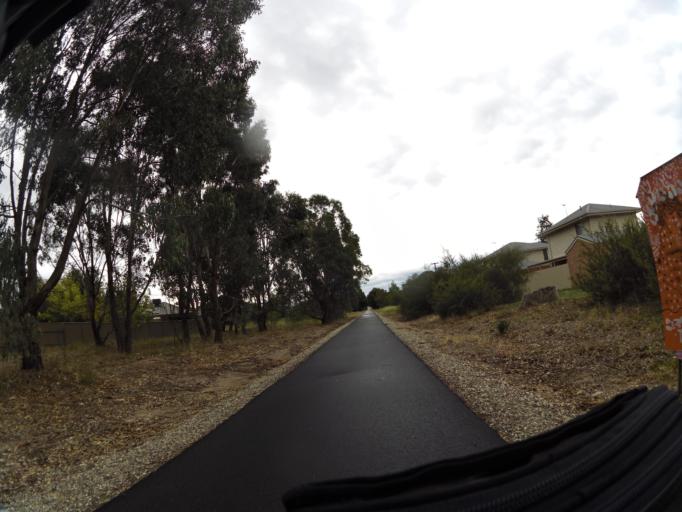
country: AU
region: Victoria
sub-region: Wodonga
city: Wodonga
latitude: -36.1283
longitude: 146.8957
